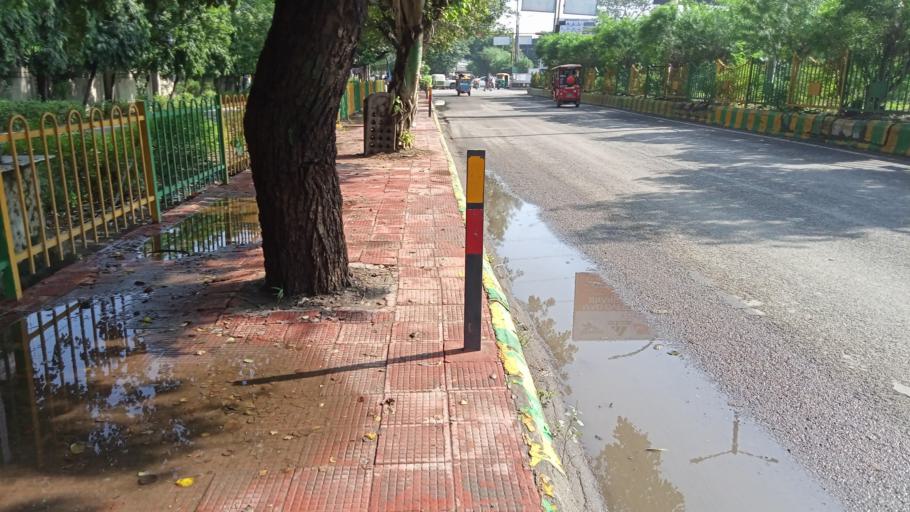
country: IN
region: Uttar Pradesh
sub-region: Ghaziabad
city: Ghaziabad
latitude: 28.6632
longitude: 77.3731
